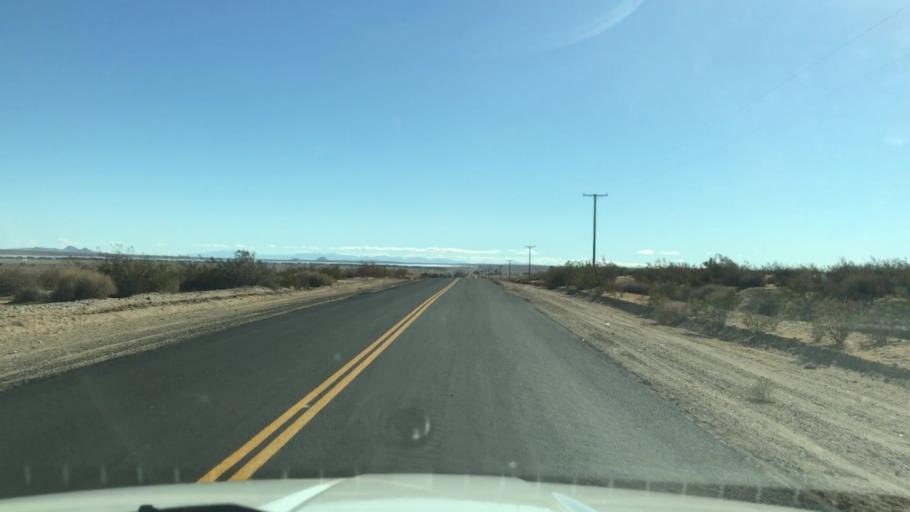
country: US
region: California
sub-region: Kern County
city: California City
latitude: 35.3064
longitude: -117.9859
